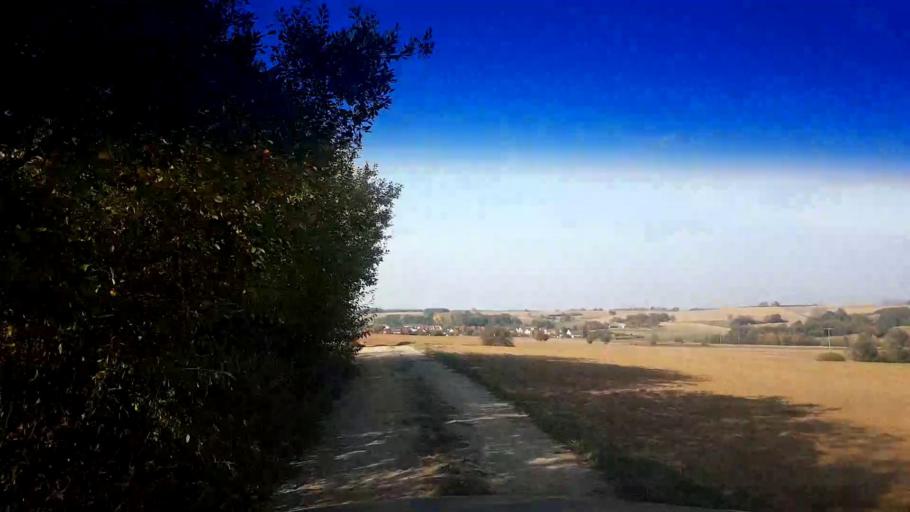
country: DE
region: Bavaria
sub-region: Upper Franconia
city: Memmelsdorf
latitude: 49.9492
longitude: 10.9599
